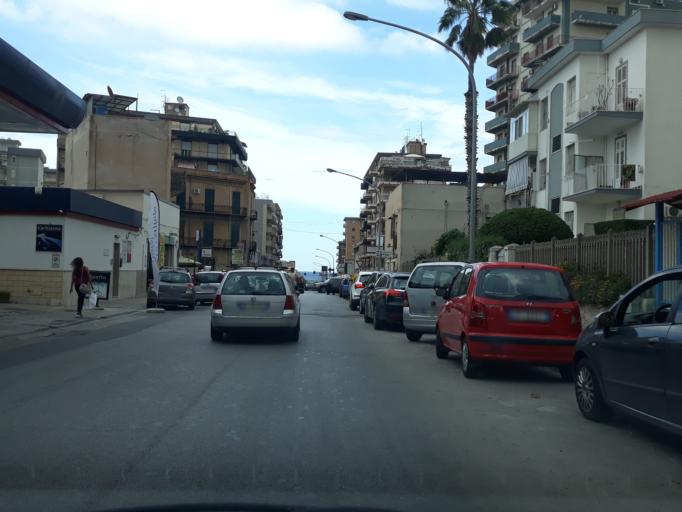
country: IT
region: Sicily
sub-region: Palermo
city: Ciaculli
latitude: 38.0982
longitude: 13.3912
